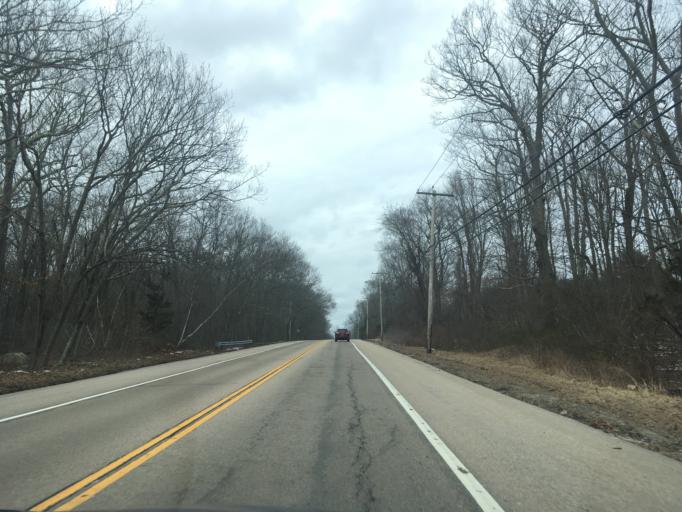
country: US
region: Rhode Island
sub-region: Kent County
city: East Greenwich
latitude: 41.6476
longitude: -71.4959
